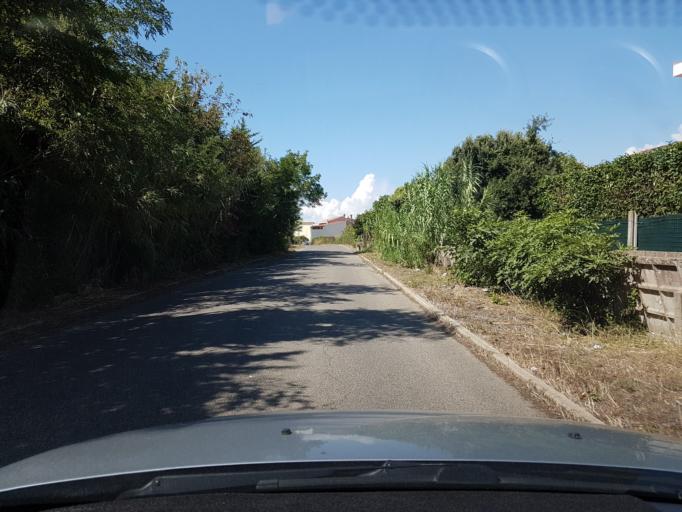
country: IT
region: Sardinia
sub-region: Provincia di Oristano
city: Donigala Fenugheddu
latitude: 39.9305
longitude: 8.5732
